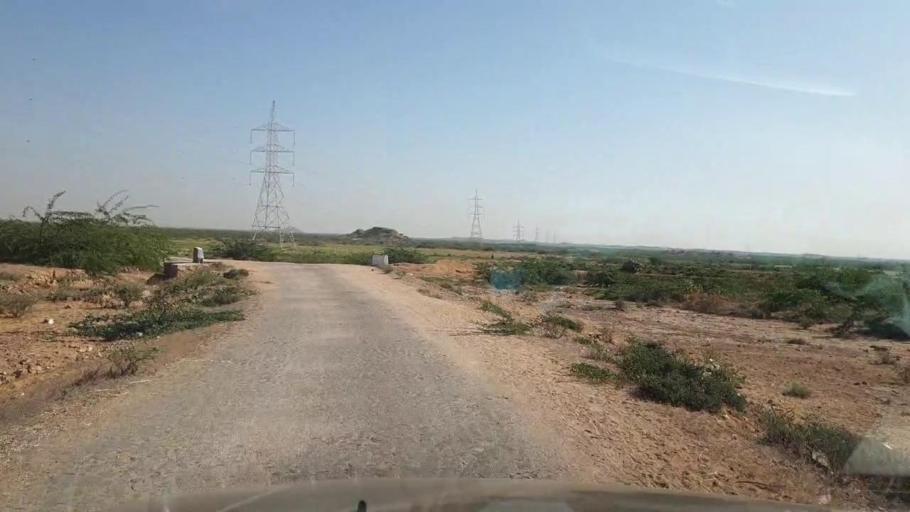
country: PK
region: Sindh
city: Thatta
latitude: 24.8712
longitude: 67.7893
